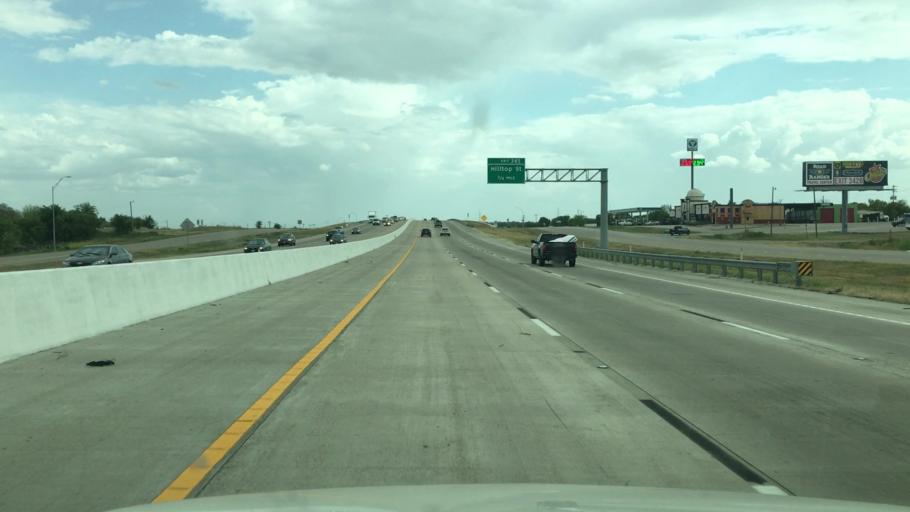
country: US
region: Texas
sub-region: McLennan County
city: West
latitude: 31.7205
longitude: -97.1027
